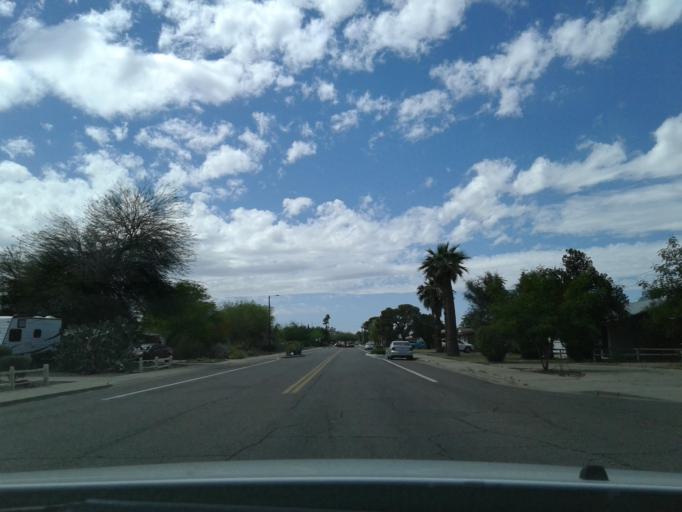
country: US
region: Arizona
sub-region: Maricopa County
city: Scottsdale
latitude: 33.4731
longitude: -111.9279
